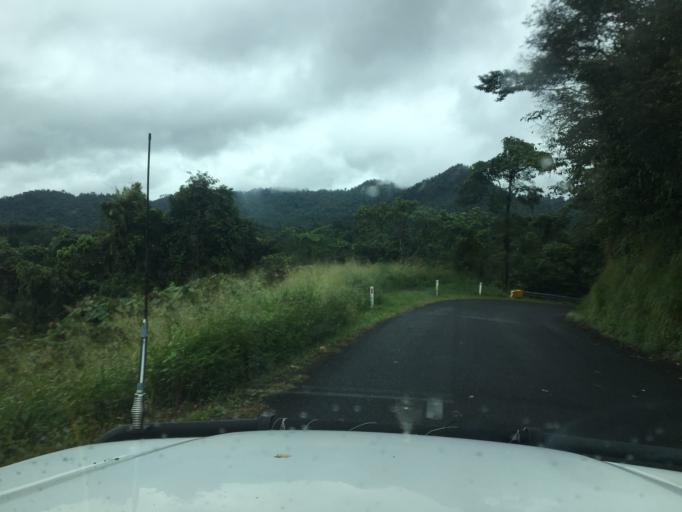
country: AU
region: Queensland
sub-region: Cassowary Coast
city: Innisfail
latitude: -17.4478
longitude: 145.8587
